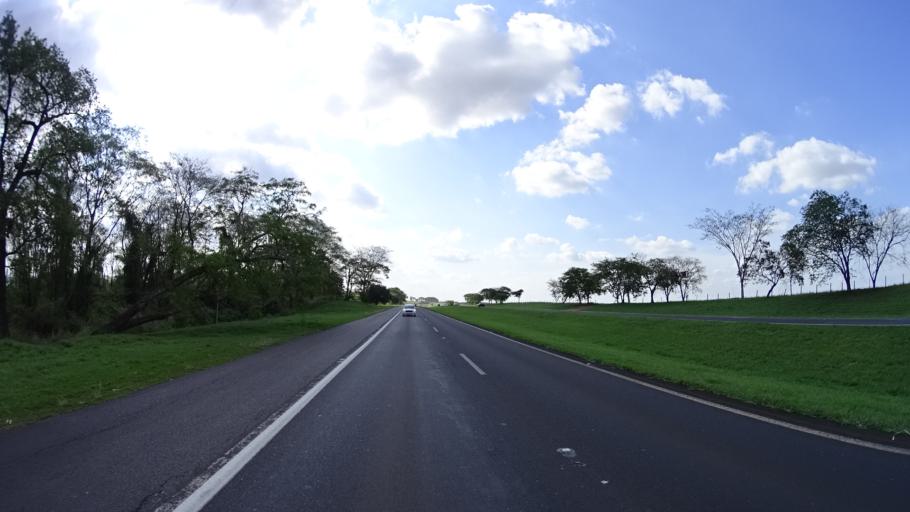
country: BR
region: Sao Paulo
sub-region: Guapiacu
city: Guapiacu
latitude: -20.9624
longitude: -49.2422
